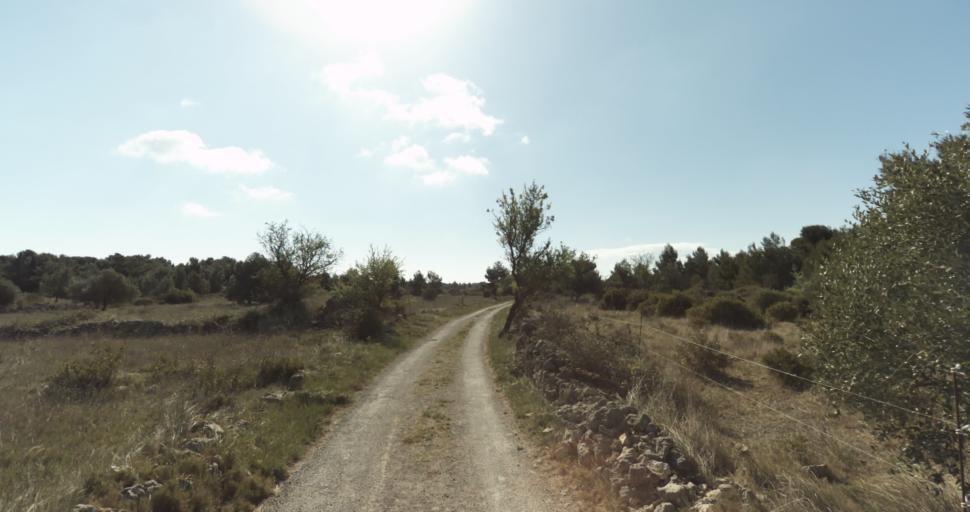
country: FR
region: Languedoc-Roussillon
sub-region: Departement de l'Aude
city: Leucate
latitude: 42.9304
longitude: 3.0293
